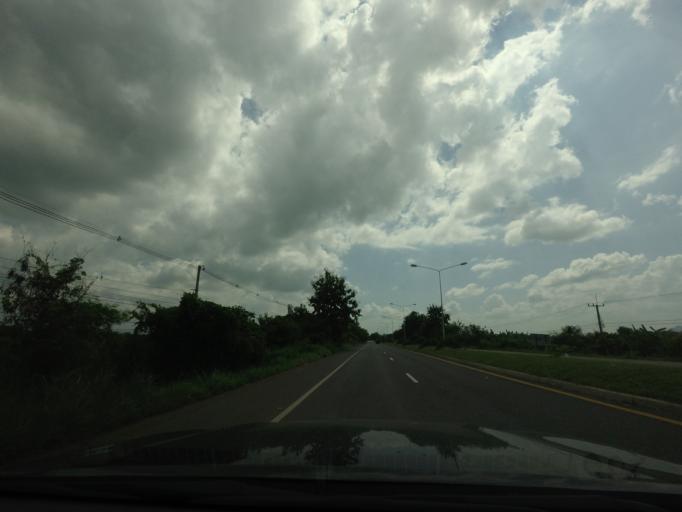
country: TH
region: Phetchabun
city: Nong Phai
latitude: 16.1881
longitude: 101.0889
